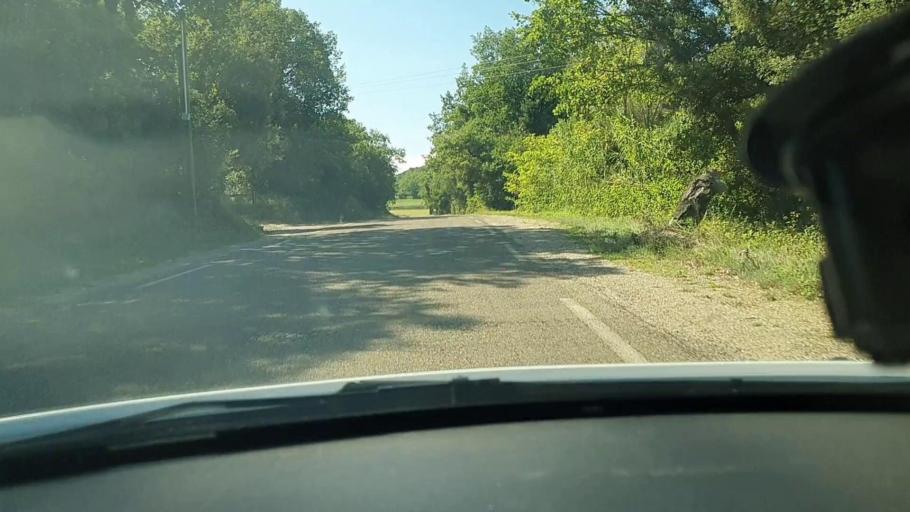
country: FR
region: Languedoc-Roussillon
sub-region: Departement du Gard
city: Saint-Paulet-de-Caisson
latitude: 44.2539
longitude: 4.5882
